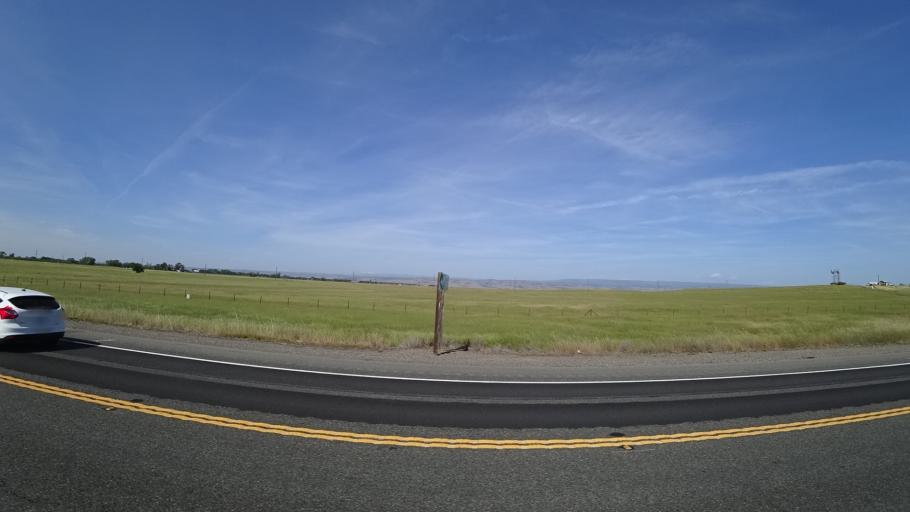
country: US
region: California
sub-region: Tehama County
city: Los Molinos
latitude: 39.9299
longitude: -122.0308
